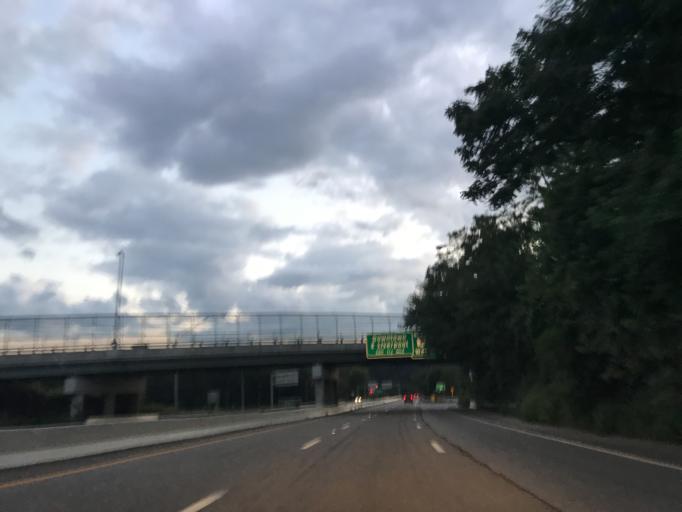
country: US
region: Ohio
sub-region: Columbiana County
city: East Liverpool
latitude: 40.6253
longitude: -80.5840
